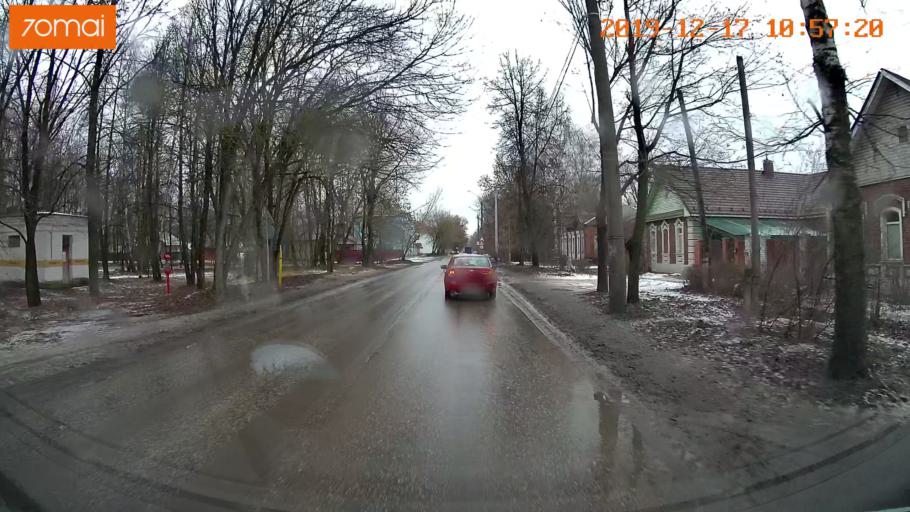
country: RU
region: Vladimir
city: Gus'-Khrustal'nyy
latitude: 55.6208
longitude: 40.6589
